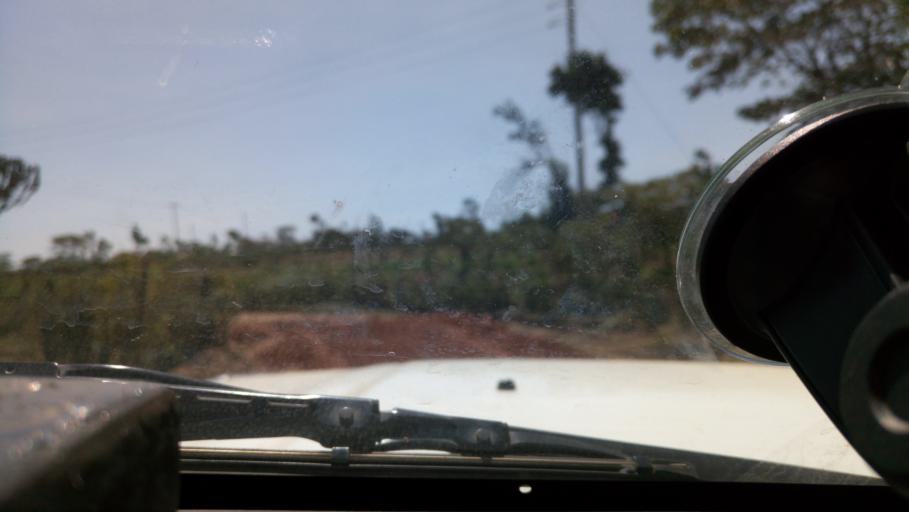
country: KE
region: Bomet
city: Bomet
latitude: -0.9573
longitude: 35.3008
